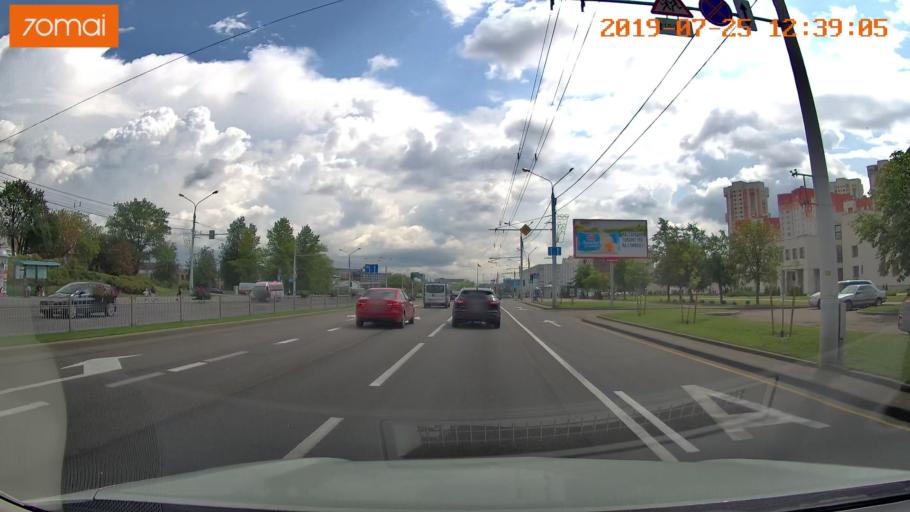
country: BY
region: Minsk
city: Novoye Medvezhino
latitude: 53.9343
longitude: 27.5013
